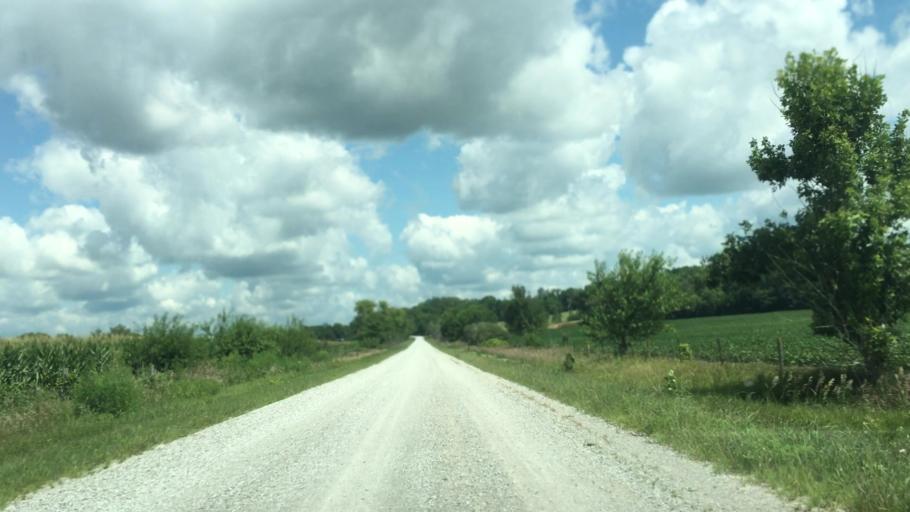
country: US
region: Iowa
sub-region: Linn County
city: Lisbon
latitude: 41.8296
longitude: -91.3906
